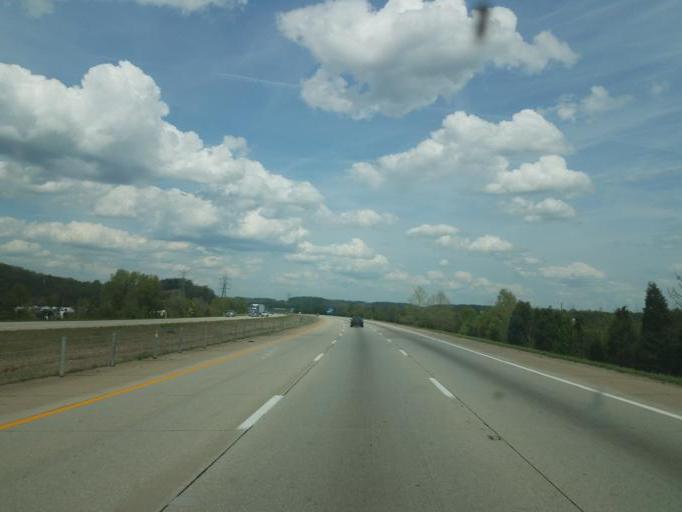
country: US
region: Kentucky
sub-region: Bullitt County
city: Shepherdsville
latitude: 37.9135
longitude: -85.6875
